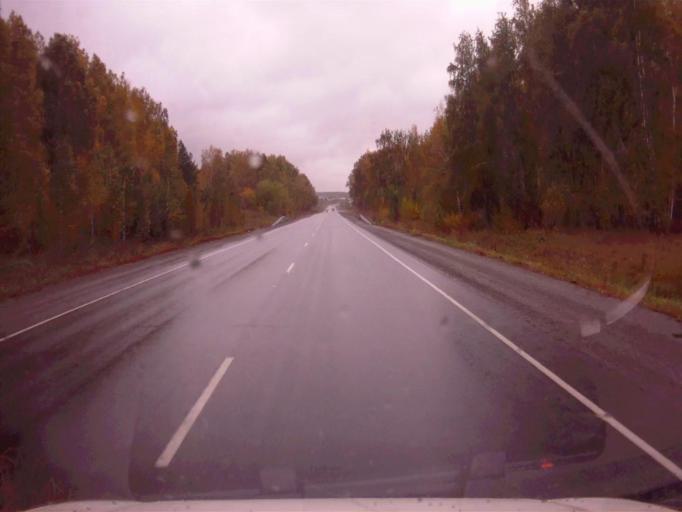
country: RU
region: Chelyabinsk
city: Roshchino
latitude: 55.3638
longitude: 61.2062
